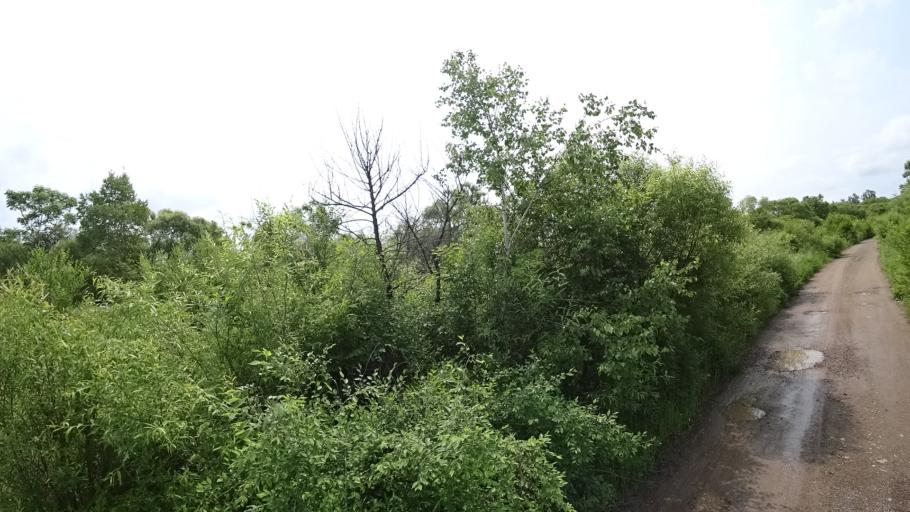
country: RU
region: Primorskiy
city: Novosysoyevka
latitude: 44.2498
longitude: 133.3732
